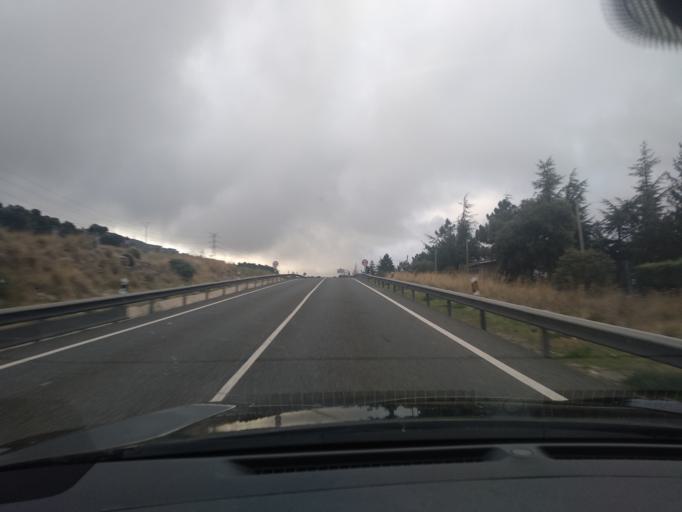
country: ES
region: Castille and Leon
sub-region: Provincia de Segovia
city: Otero de Herreros
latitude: 40.7818
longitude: -4.2105
